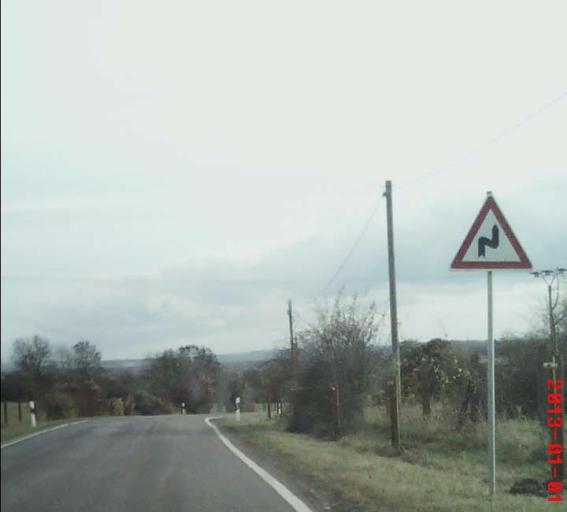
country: DE
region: Thuringia
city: Muehlhausen
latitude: 51.2272
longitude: 10.4247
